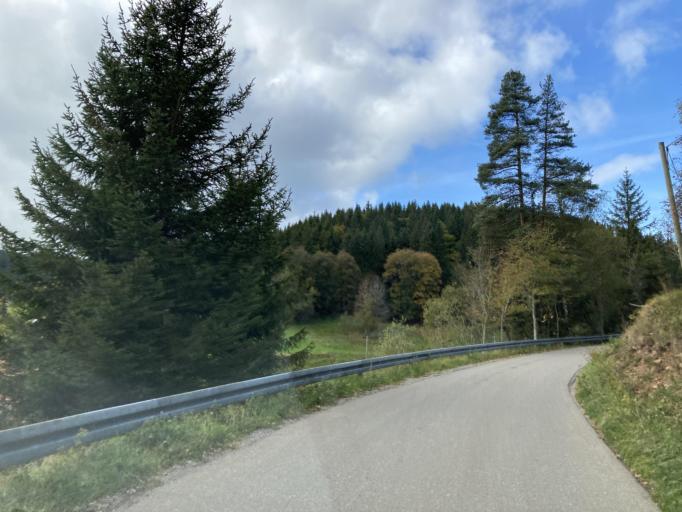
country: DE
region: Baden-Wuerttemberg
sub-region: Freiburg Region
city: Vohrenbach
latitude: 48.0590
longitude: 8.2862
